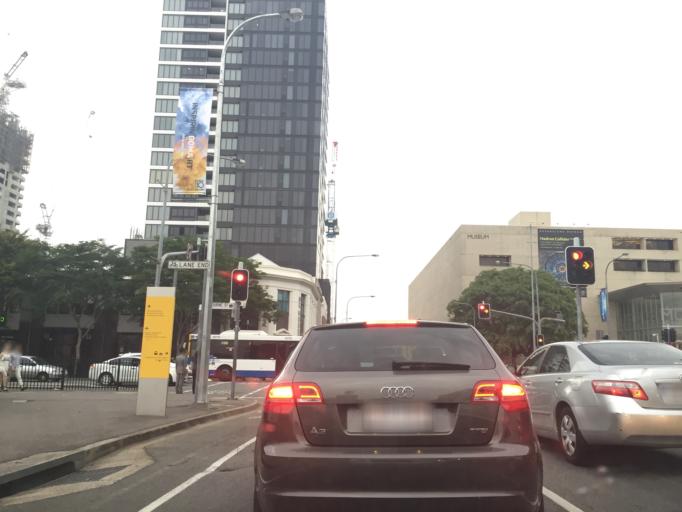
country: AU
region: Queensland
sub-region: Brisbane
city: South Brisbane
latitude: -27.4743
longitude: 153.0185
